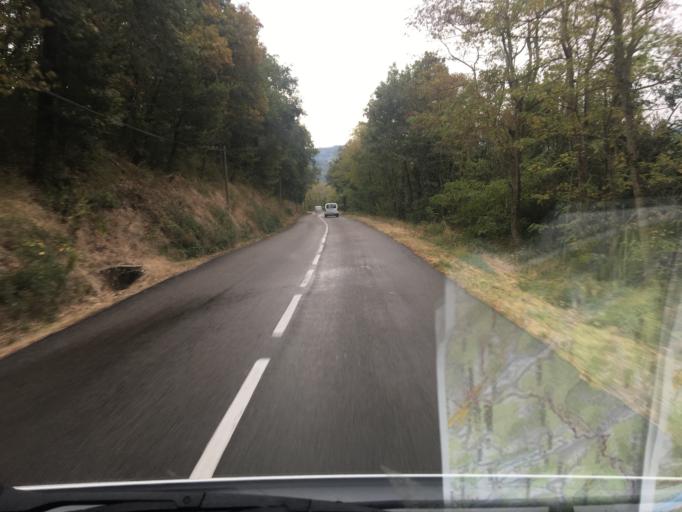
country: FR
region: Rhone-Alpes
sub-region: Departement de l'Ardeche
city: Saint-Felicien
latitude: 45.0571
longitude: 4.7063
